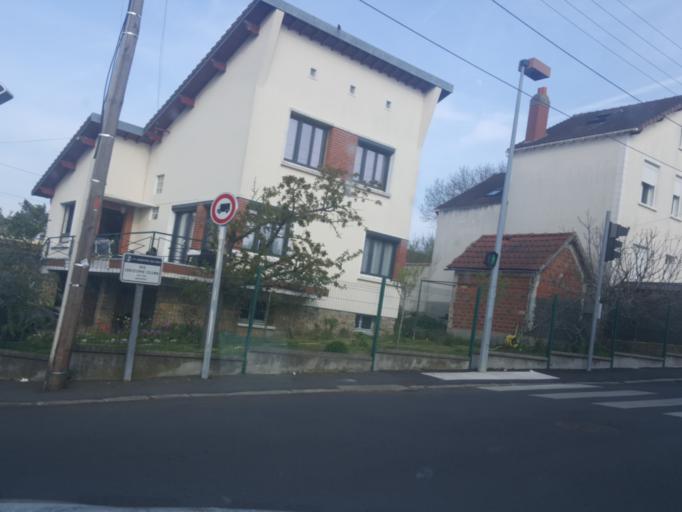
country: FR
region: Ile-de-France
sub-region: Departement de l'Essonne
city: Villiers-sur-Orge
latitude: 48.6494
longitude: 2.3052
